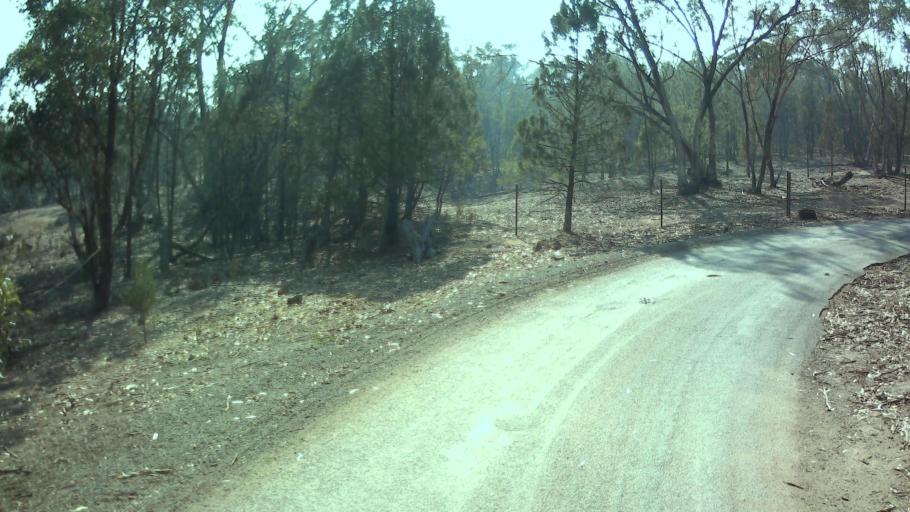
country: AU
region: New South Wales
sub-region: Weddin
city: Grenfell
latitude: -33.8928
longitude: 148.1790
